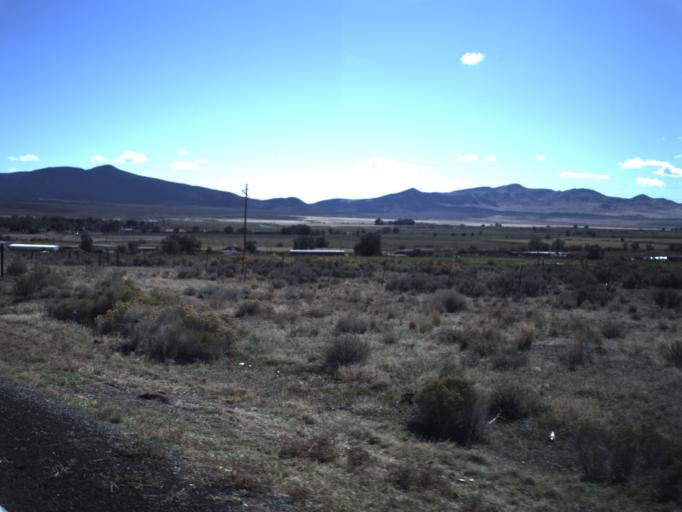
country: US
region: Utah
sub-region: Beaver County
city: Milford
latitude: 38.2330
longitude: -112.9337
